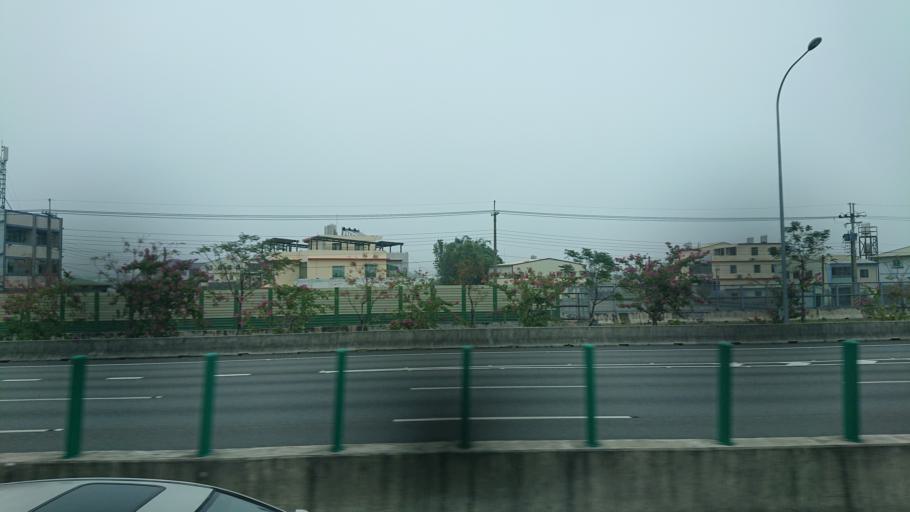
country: TW
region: Taiwan
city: Fengyuan
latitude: 24.2981
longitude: 120.6965
